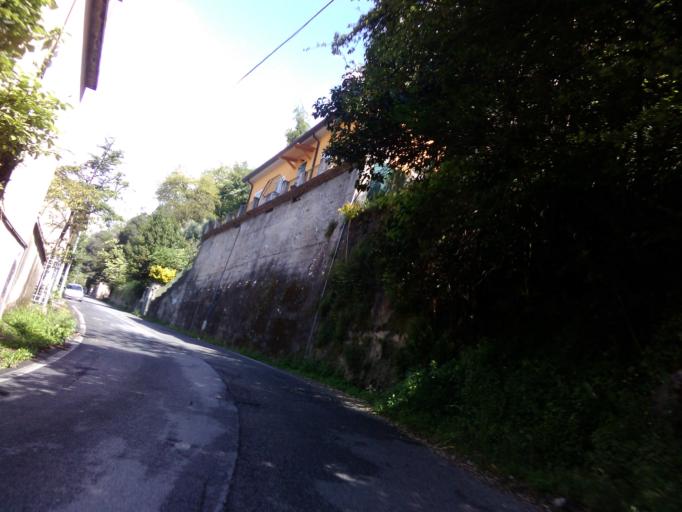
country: IT
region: Tuscany
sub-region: Provincia di Massa-Carrara
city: Carrara
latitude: 44.0765
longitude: 10.1066
